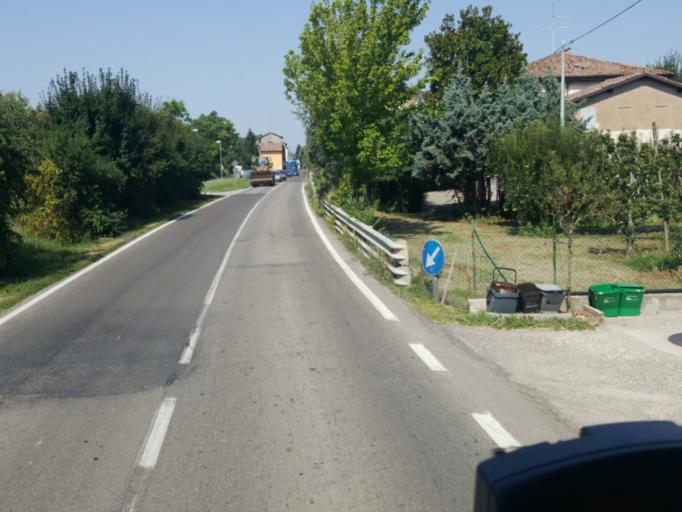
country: IT
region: Emilia-Romagna
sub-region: Provincia di Modena
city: Ca' di Sola
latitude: 44.5414
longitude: 10.9594
